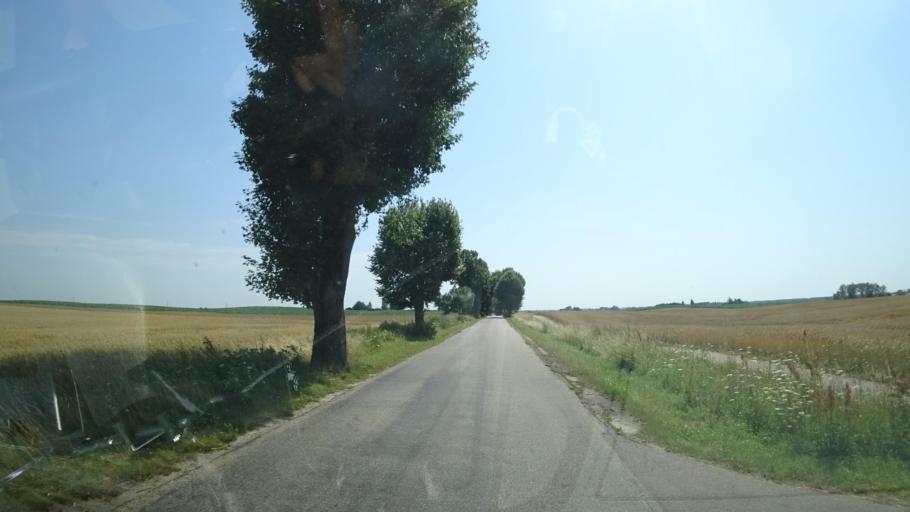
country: PL
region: Pomeranian Voivodeship
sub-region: Powiat chojnicki
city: Brusy
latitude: 53.8786
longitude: 17.6505
